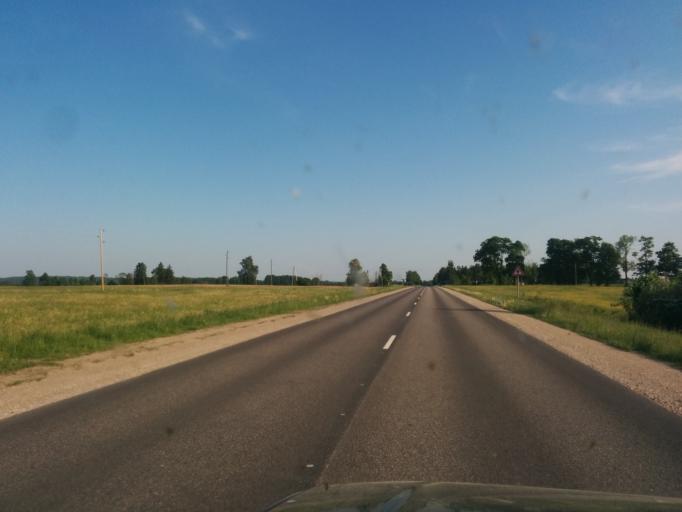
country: LV
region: Talsu Rajons
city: Talsi
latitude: 57.2843
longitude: 22.5734
